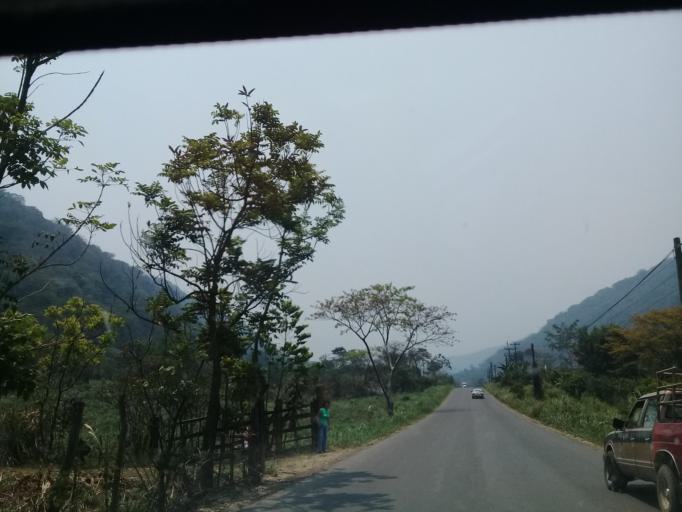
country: MX
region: Veracruz
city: Tezonapa
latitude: 18.6183
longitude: -96.6985
